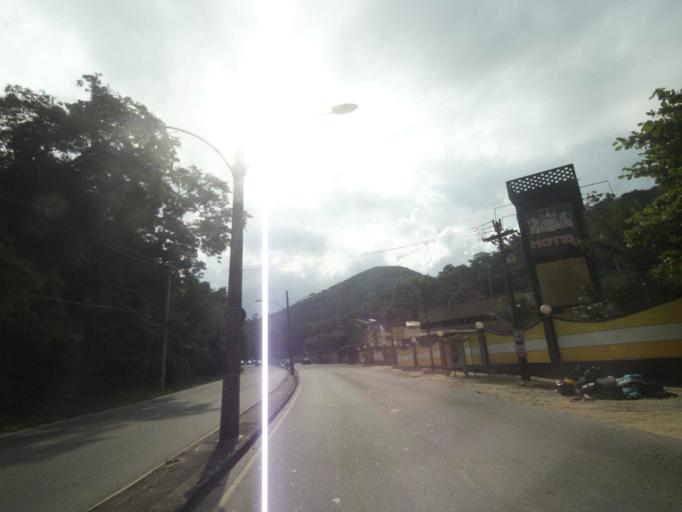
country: BR
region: Rio de Janeiro
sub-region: Sao Joao De Meriti
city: Sao Joao de Meriti
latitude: -22.9005
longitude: -43.3824
